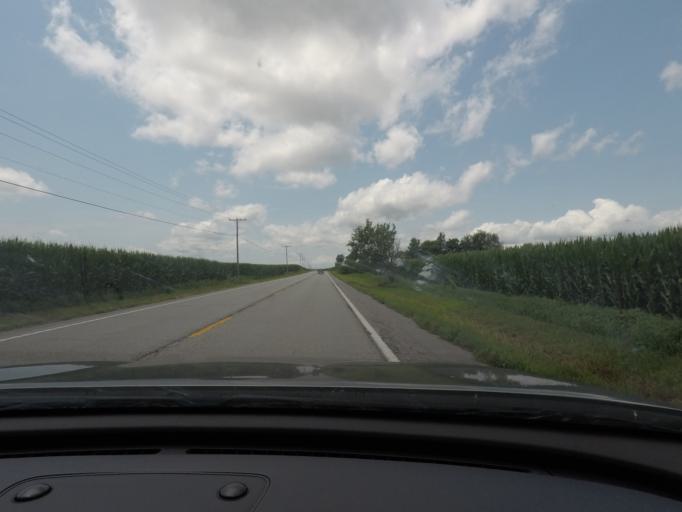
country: US
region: Missouri
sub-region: Saline County
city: Marshall
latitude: 39.1940
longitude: -93.3720
